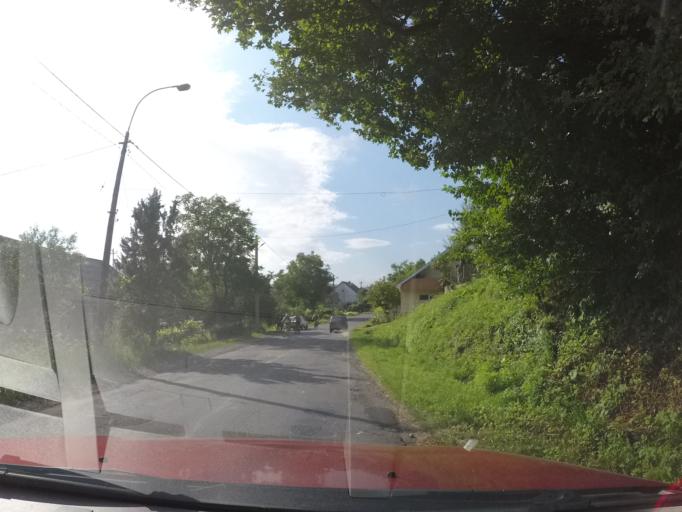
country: UA
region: Zakarpattia
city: Velykyi Bereznyi
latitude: 48.9139
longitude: 22.4598
